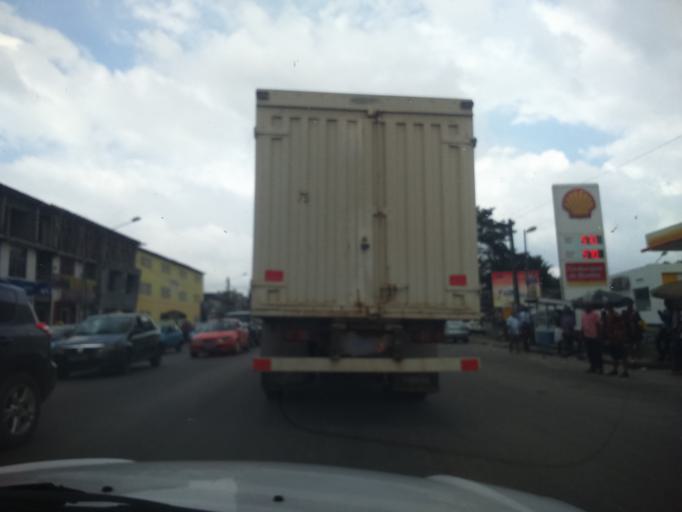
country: CI
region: Lagunes
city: Abidjan
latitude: 5.3469
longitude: -4.0634
